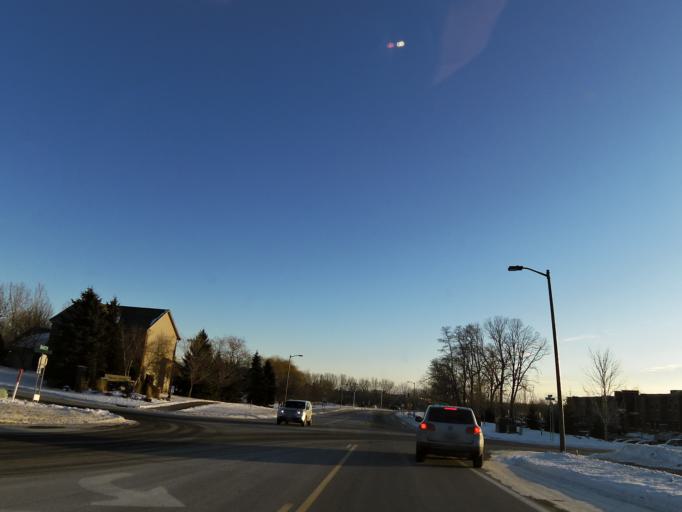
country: US
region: Minnesota
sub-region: Hennepin County
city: Shorewood
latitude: 44.8509
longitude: -93.5819
